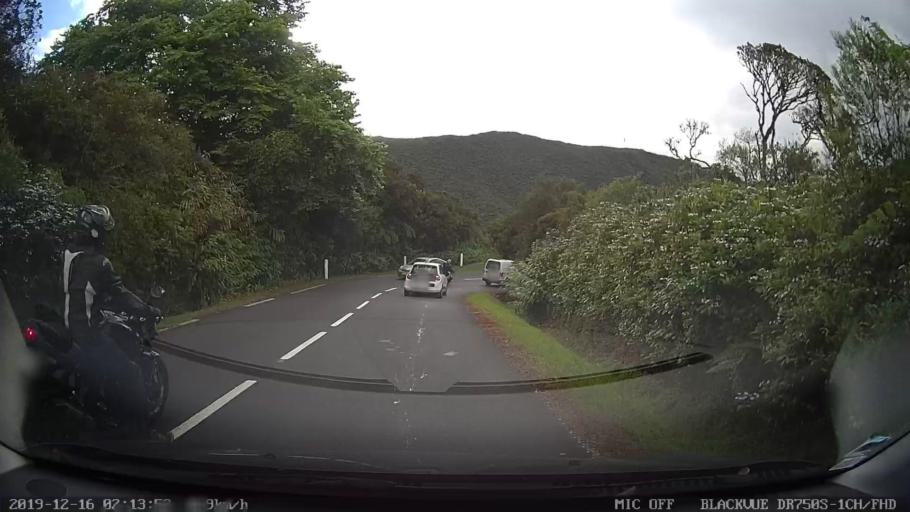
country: RE
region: Reunion
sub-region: Reunion
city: Cilaos
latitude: -21.1600
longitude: 55.5964
